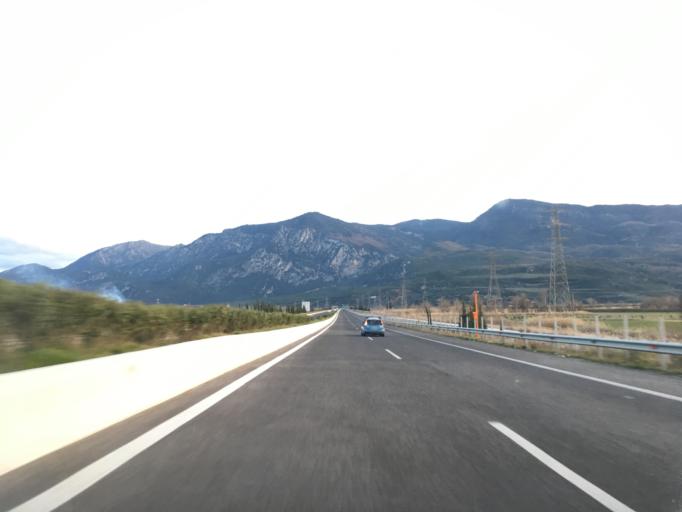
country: GR
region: Central Greece
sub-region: Nomos Fthiotidos
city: Anthili
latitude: 38.8252
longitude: 22.4866
